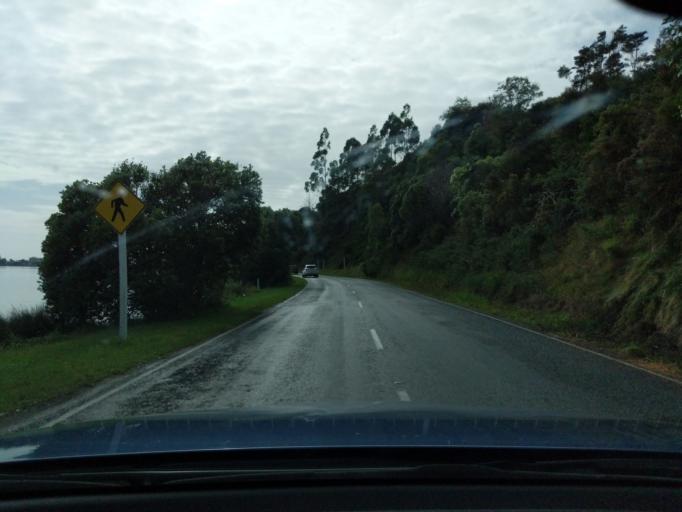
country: NZ
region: Tasman
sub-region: Tasman District
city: Takaka
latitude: -40.6809
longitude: 172.6744
